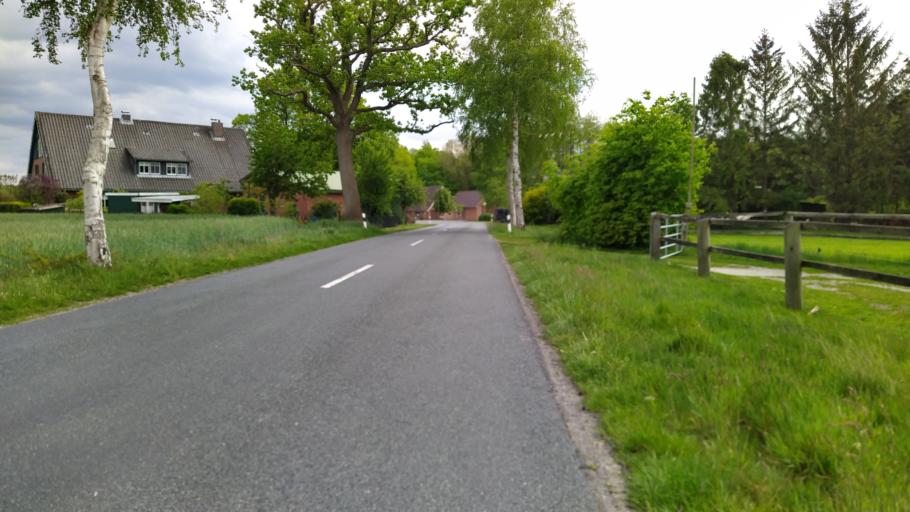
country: DE
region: Lower Saxony
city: Brest
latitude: 53.4356
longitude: 9.3532
